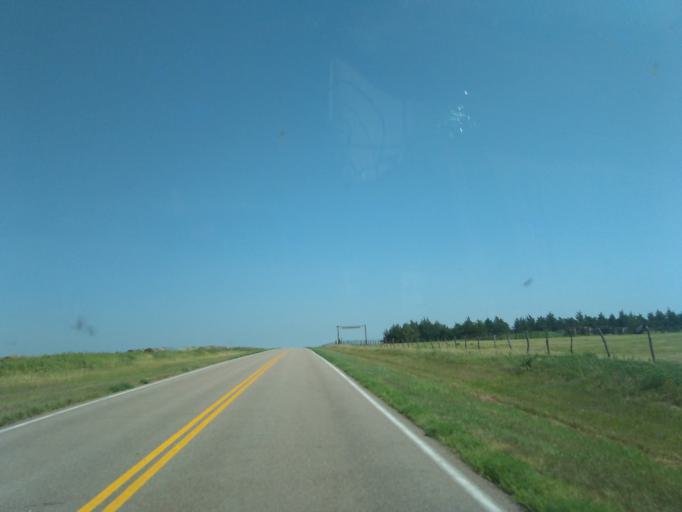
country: US
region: Nebraska
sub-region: Dundy County
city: Benkelman
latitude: 39.9074
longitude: -101.5412
